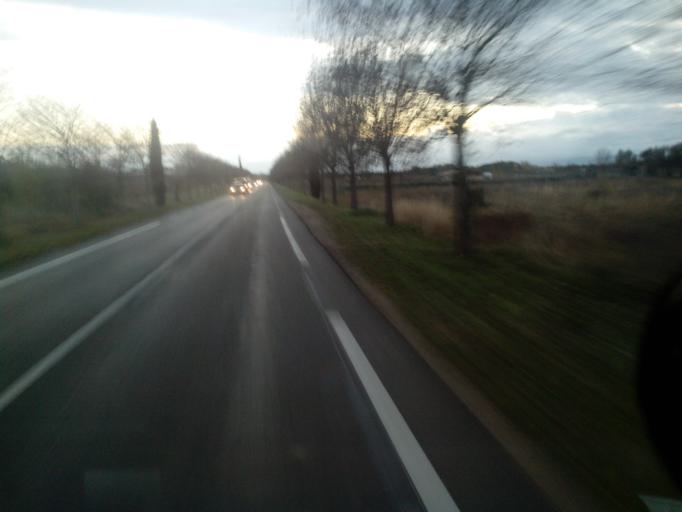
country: FR
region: Languedoc-Roussillon
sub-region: Departement de l'Herault
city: Aniane
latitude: 43.6774
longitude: 3.5752
